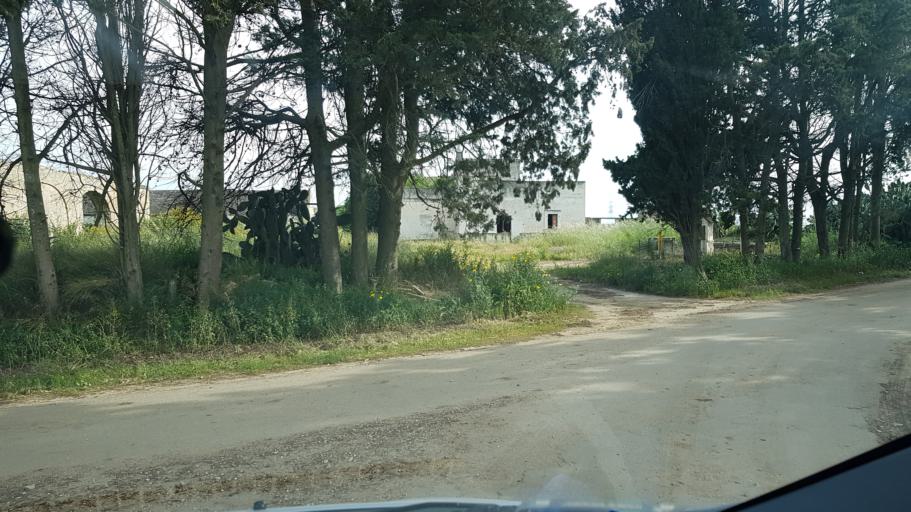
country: IT
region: Apulia
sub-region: Provincia di Brindisi
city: Tuturano
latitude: 40.5613
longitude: 17.9180
